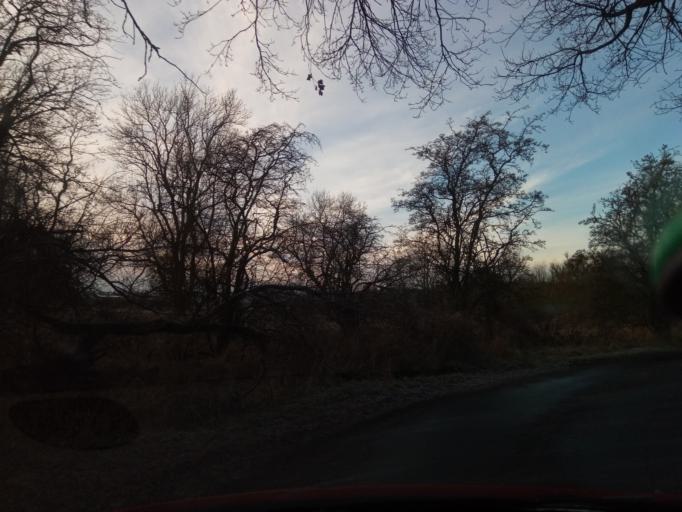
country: GB
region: Scotland
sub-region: The Scottish Borders
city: Hawick
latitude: 55.4537
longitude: -2.7144
